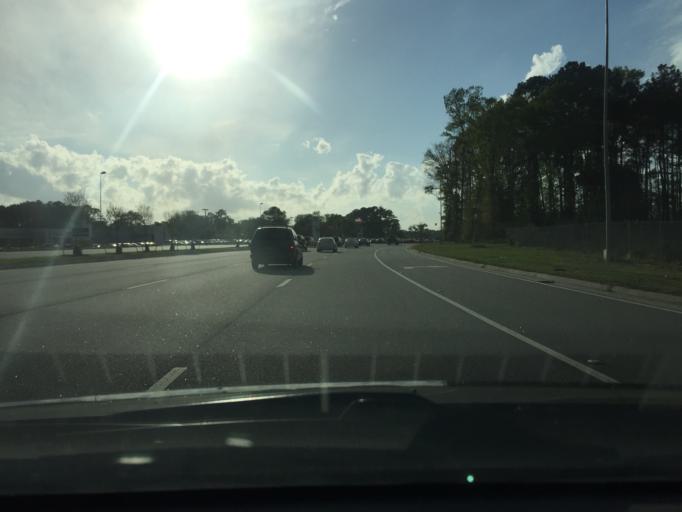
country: US
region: Georgia
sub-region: Chatham County
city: Montgomery
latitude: 31.9792
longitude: -81.1393
